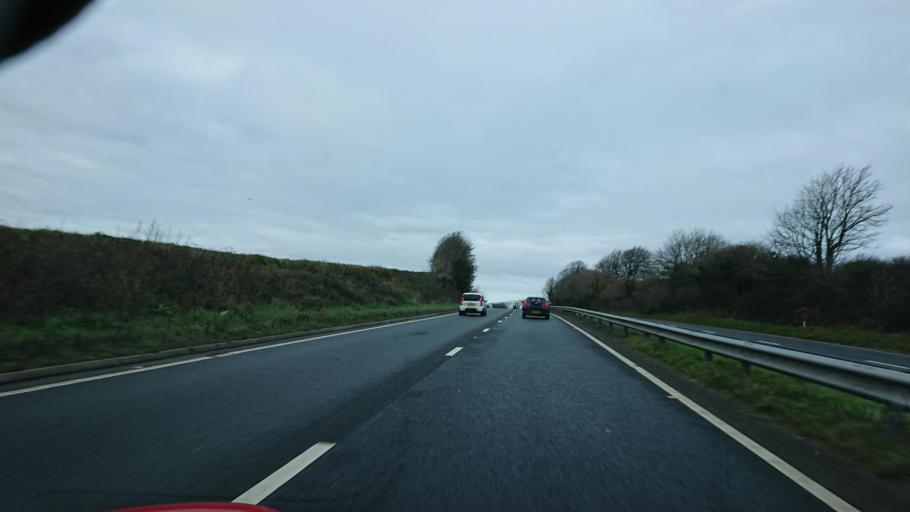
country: GB
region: England
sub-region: Cornwall
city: Liskeard
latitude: 50.4374
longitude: -4.4410
